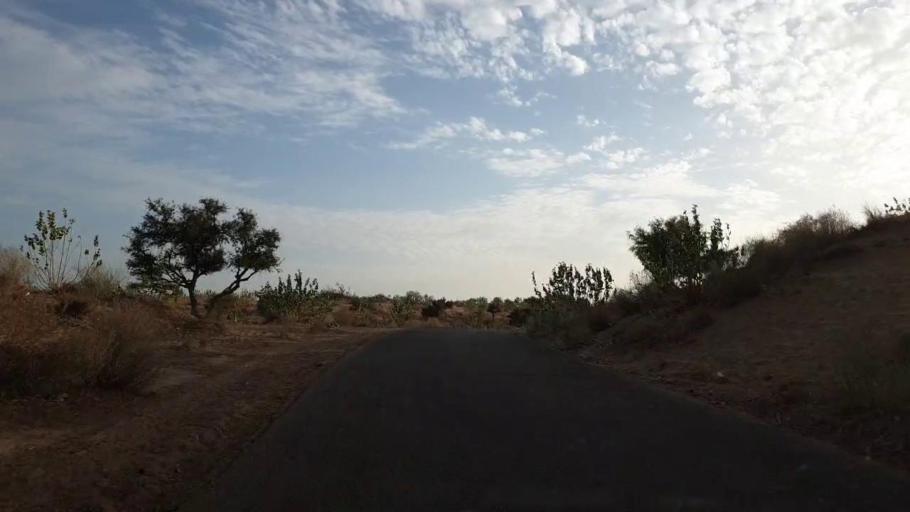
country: PK
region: Sindh
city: Umarkot
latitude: 25.1276
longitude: 70.0075
